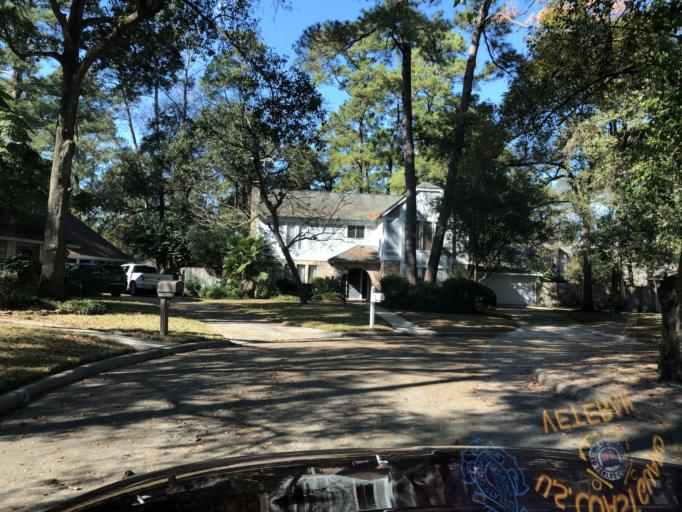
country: US
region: Texas
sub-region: Harris County
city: Tomball
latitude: 30.0263
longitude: -95.5527
